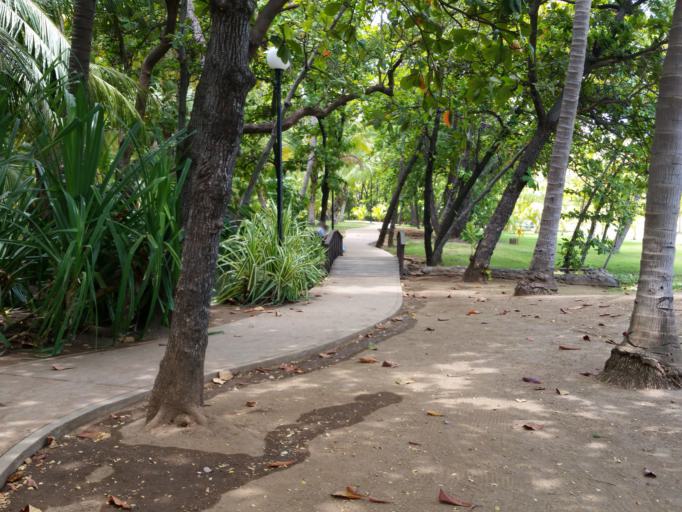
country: NI
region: Managua
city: Masachapa
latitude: 11.8067
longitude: -86.5207
